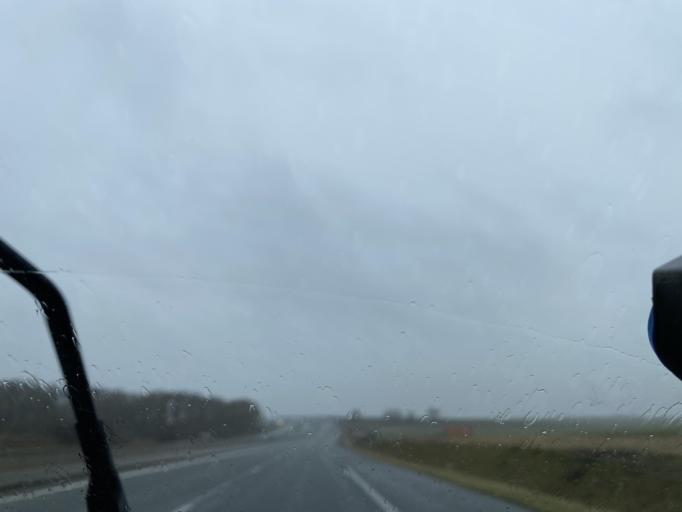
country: FR
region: Centre
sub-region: Departement d'Eure-et-Loir
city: Villemeux-sur-Eure
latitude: 48.6011
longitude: 1.4222
